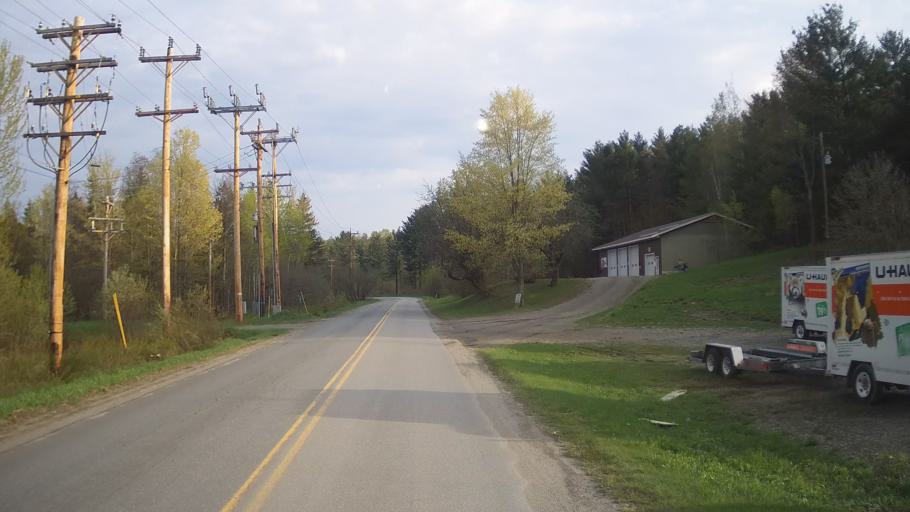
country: US
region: Vermont
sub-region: Orleans County
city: Newport
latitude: 44.9473
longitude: -72.4381
